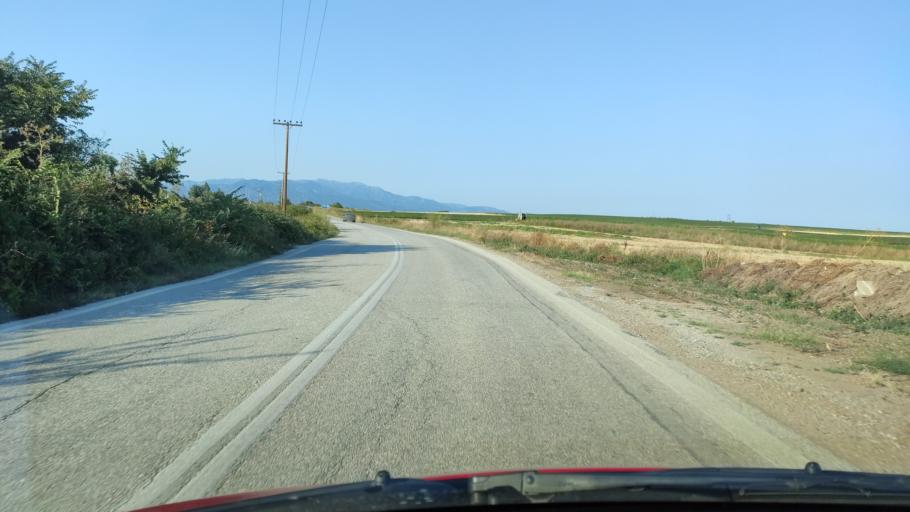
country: GR
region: East Macedonia and Thrace
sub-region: Nomos Rodopis
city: Iasmos
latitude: 41.0006
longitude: 25.1744
